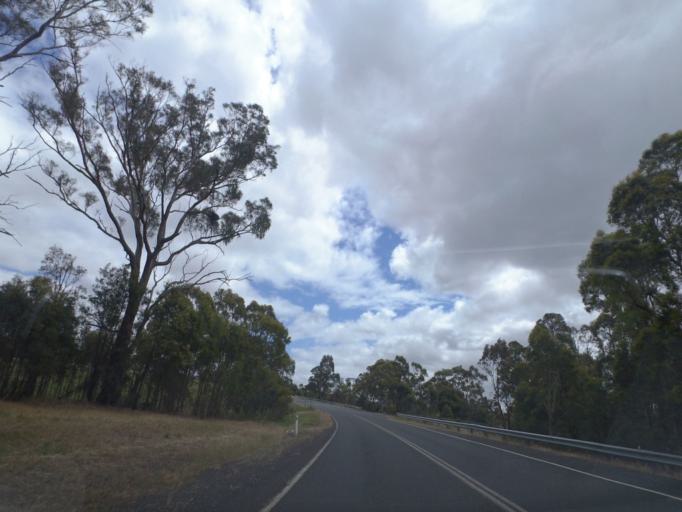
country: AU
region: Victoria
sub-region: Whittlesea
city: Whittlesea
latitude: -37.2890
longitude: 145.0578
